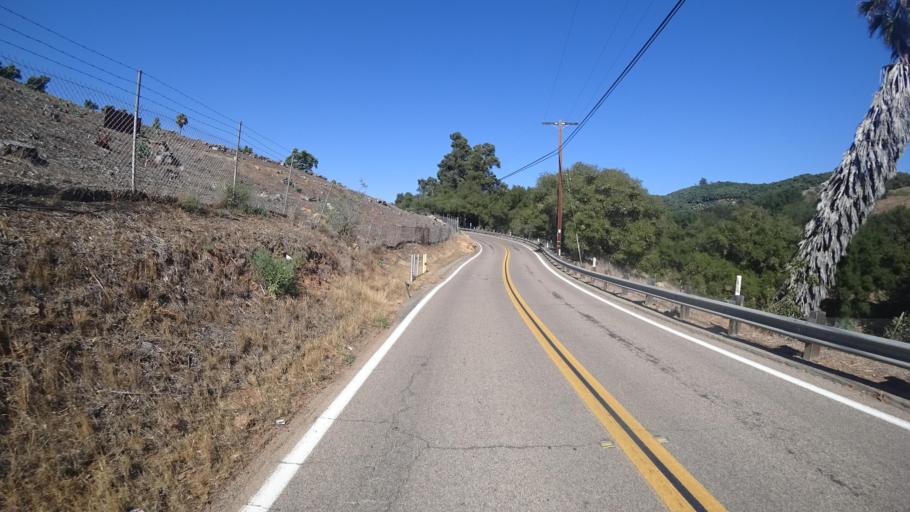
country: US
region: California
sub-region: San Diego County
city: Hidden Meadows
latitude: 33.2624
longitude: -117.1349
